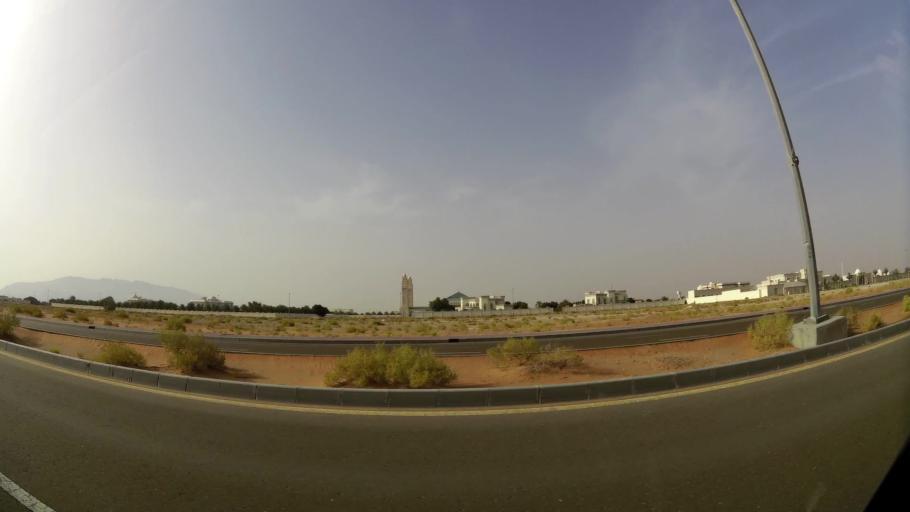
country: AE
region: Abu Dhabi
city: Al Ain
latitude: 24.1265
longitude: 55.6695
